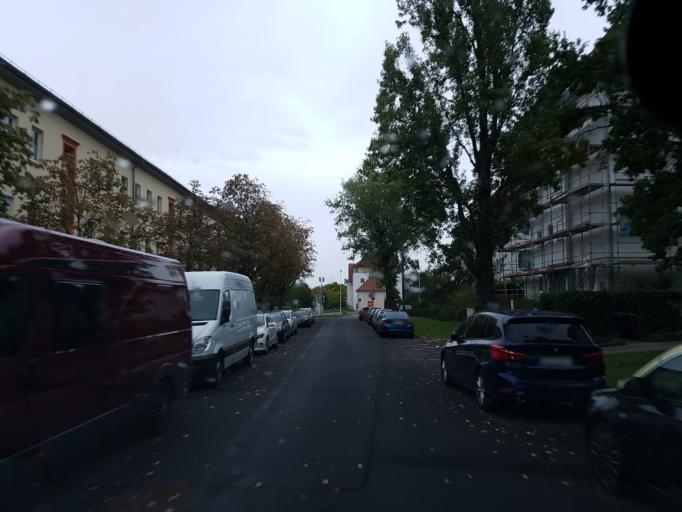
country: DE
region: Saxony
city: Riesa
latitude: 51.2998
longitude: 13.3062
